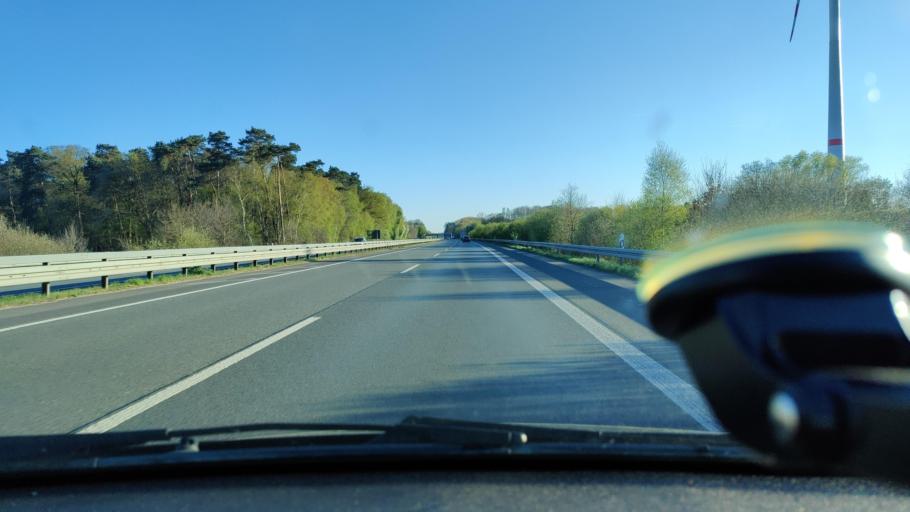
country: DE
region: North Rhine-Westphalia
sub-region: Regierungsbezirk Munster
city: Velen
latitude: 51.9141
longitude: 7.0259
